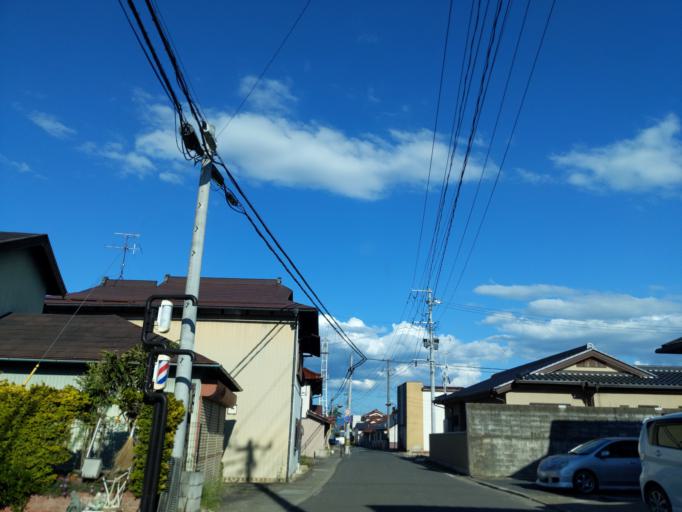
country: JP
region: Fukushima
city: Sukagawa
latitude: 37.3298
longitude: 140.3227
